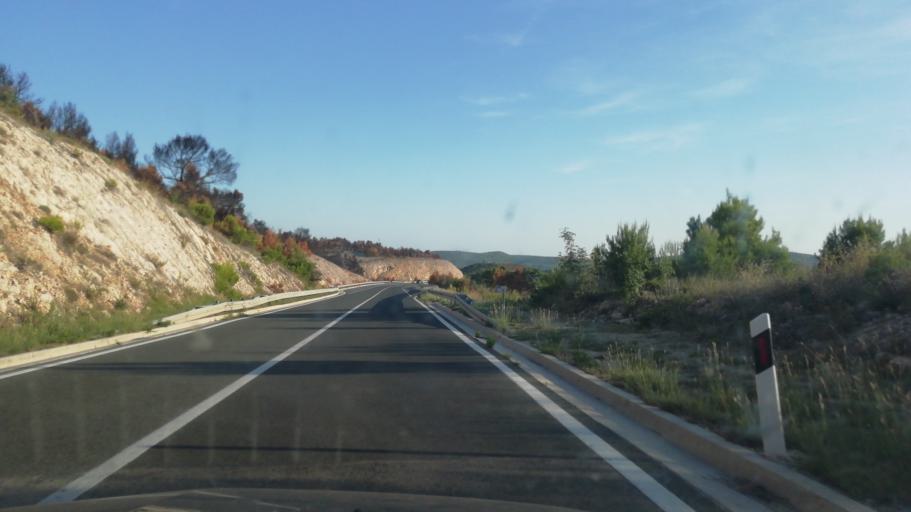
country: HR
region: Sibensko-Kniniska
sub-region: Grad Sibenik
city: Sibenik
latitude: 43.7666
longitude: 15.9380
